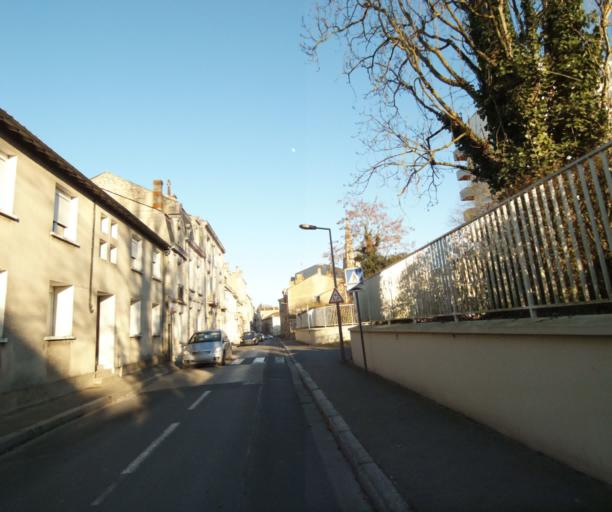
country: FR
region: Poitou-Charentes
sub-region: Departement des Deux-Sevres
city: Niort
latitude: 46.3230
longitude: -0.4693
